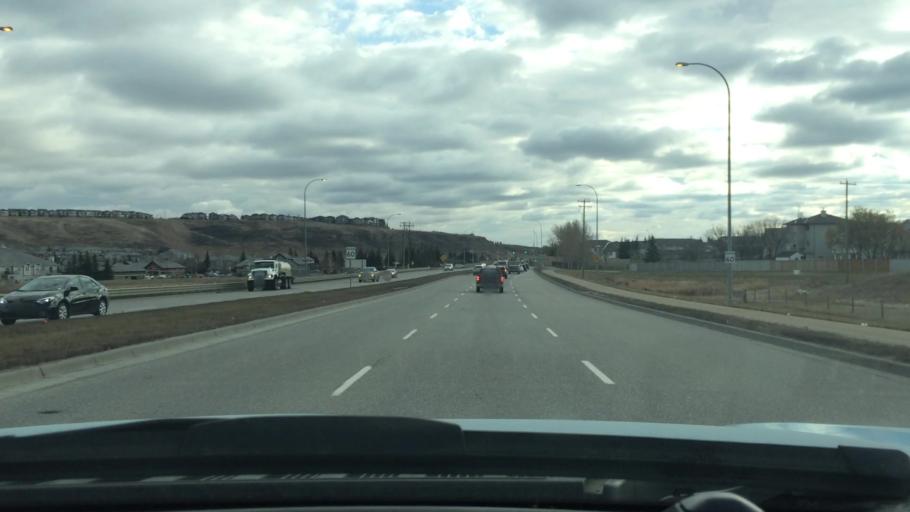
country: CA
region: Alberta
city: Calgary
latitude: 51.1550
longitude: -114.1105
